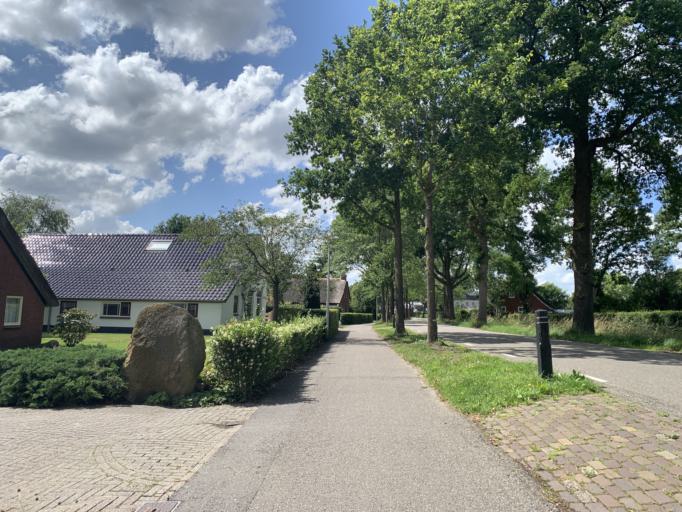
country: NL
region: Groningen
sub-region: Gemeente Haren
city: Haren
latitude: 53.1630
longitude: 6.6341
